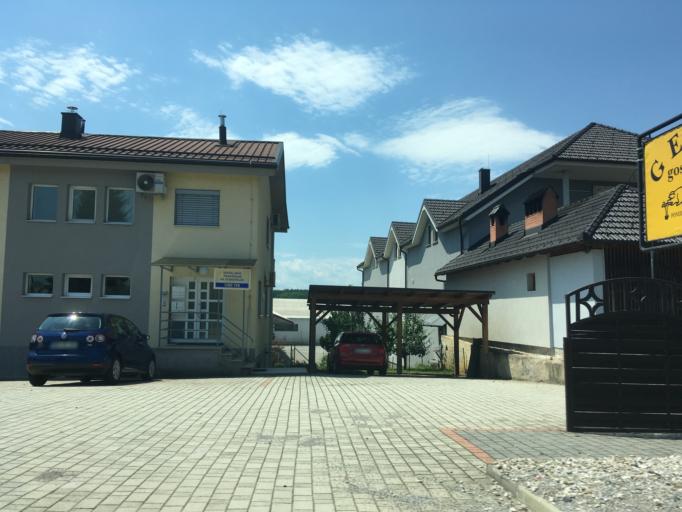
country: SI
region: Metlika
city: Metlika
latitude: 45.6420
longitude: 15.3207
